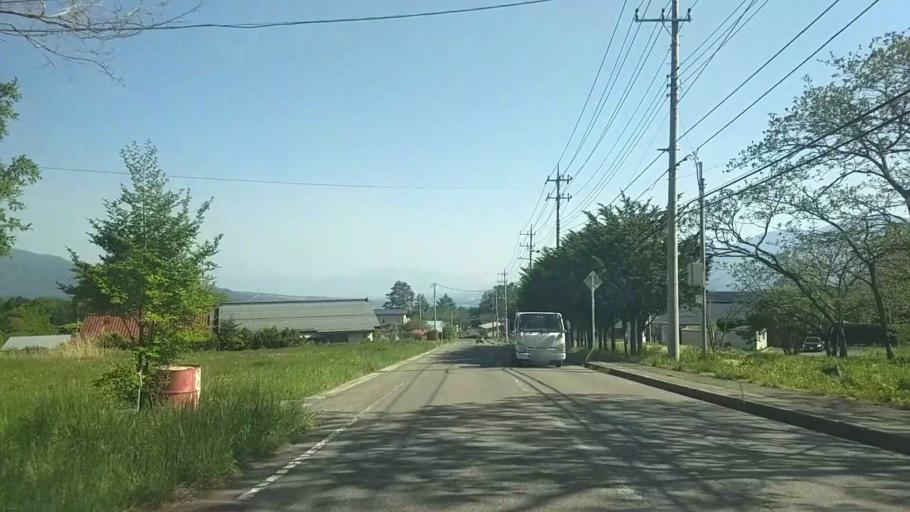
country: JP
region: Yamanashi
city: Nirasaki
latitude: 35.9004
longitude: 138.4098
